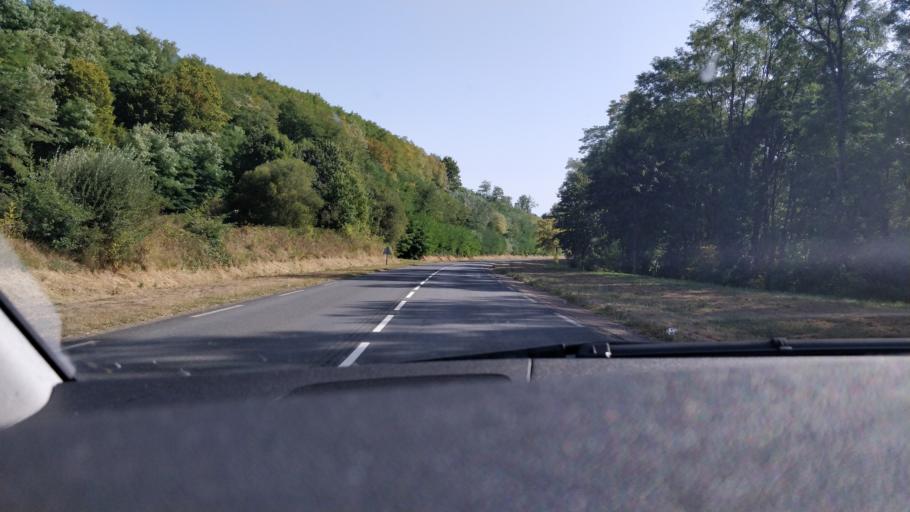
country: FR
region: Limousin
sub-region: Departement de la Correze
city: Uzerche
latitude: 45.4565
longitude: 1.5575
